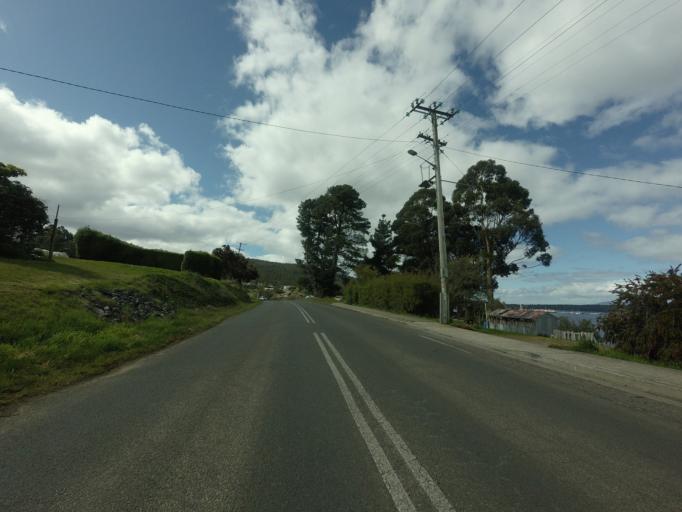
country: AU
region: Tasmania
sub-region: Huon Valley
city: Cygnet
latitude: -43.3181
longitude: 147.0100
